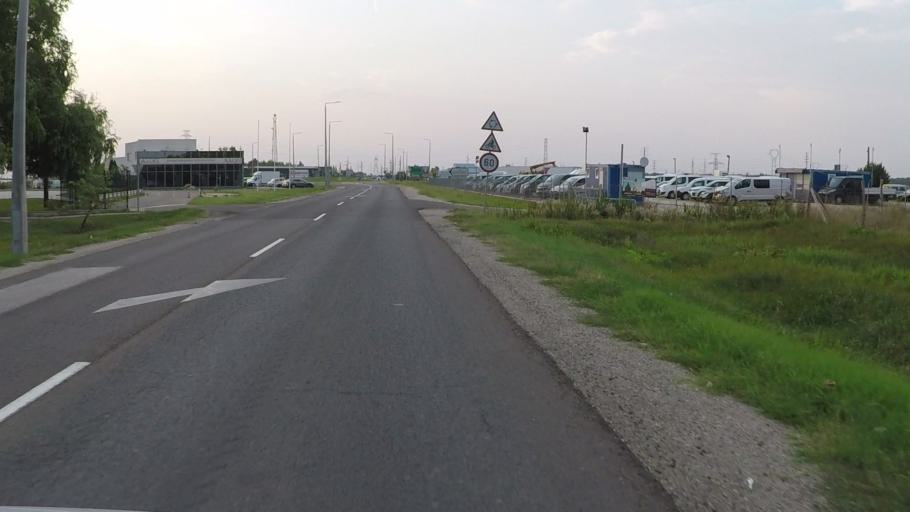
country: HU
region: Jasz-Nagykun-Szolnok
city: Szolnok
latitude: 47.1997
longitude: 20.1614
